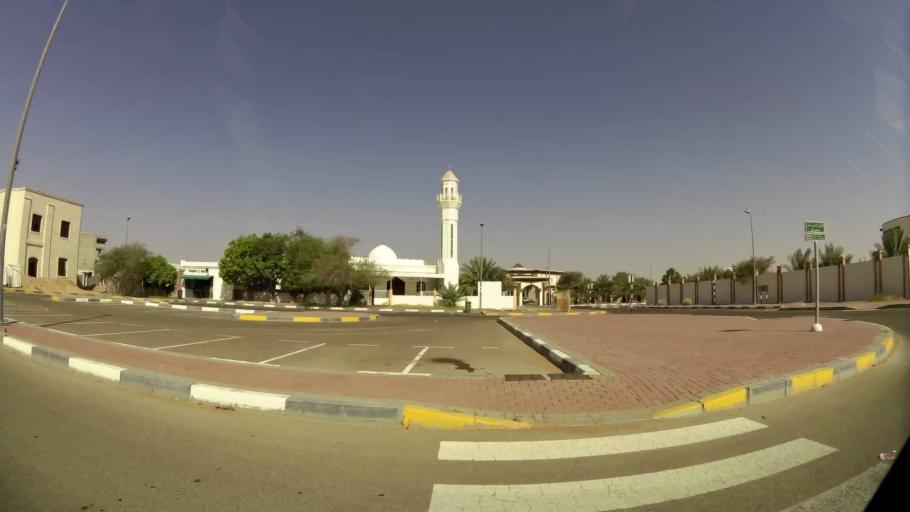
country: OM
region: Al Buraimi
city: Al Buraymi
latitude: 24.3356
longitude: 55.7934
